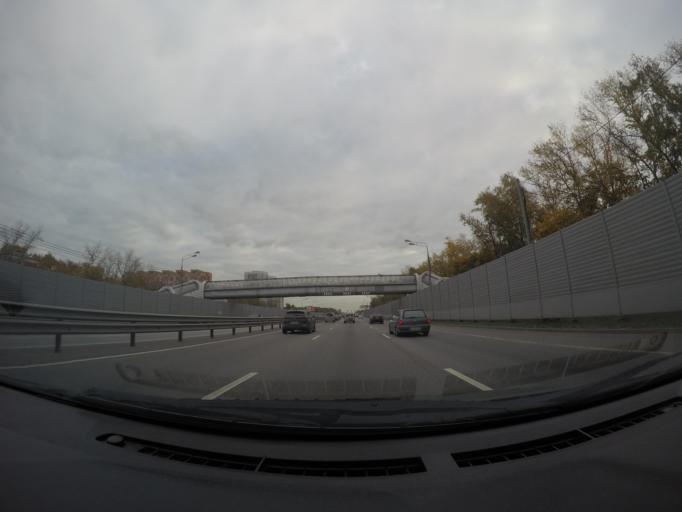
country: RU
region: Moskovskaya
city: Balashikha
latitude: 55.7980
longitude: 37.9783
